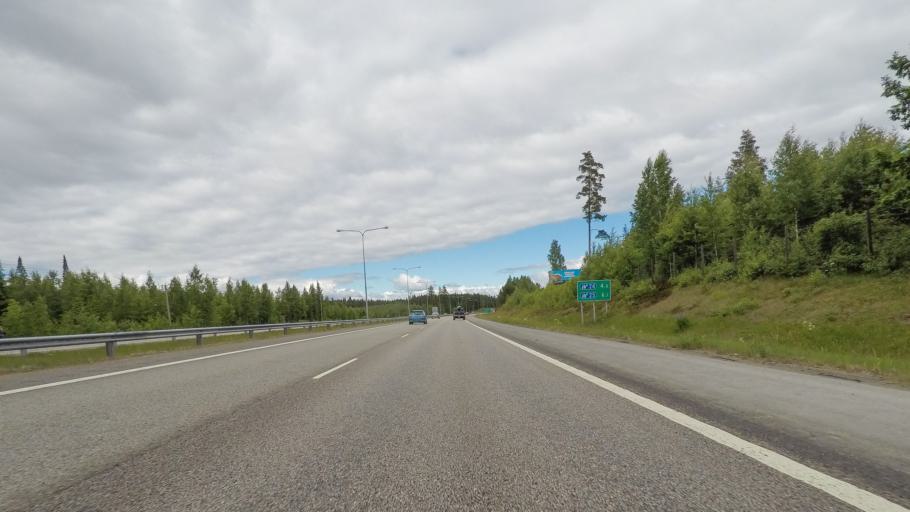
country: FI
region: Paijanne Tavastia
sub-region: Lahti
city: Heinola
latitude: 61.2018
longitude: 26.0026
